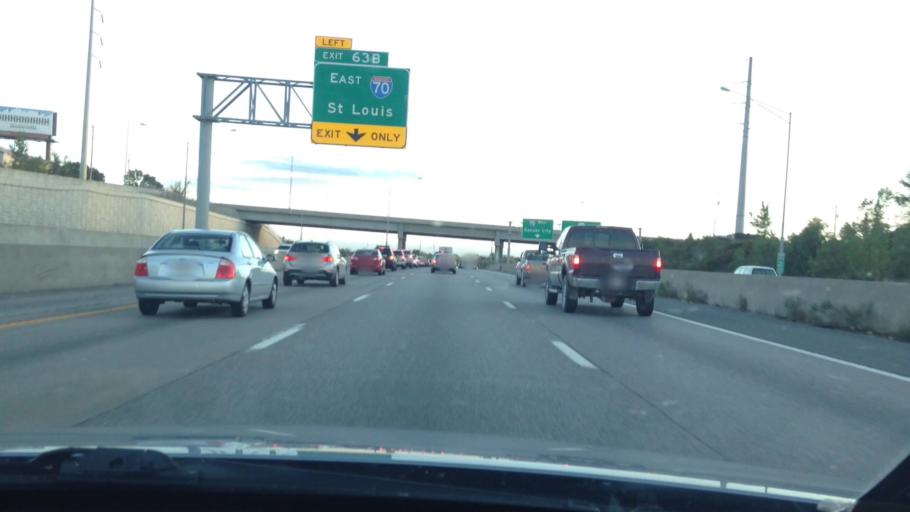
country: US
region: Missouri
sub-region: Jackson County
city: Raytown
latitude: 39.0652
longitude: -94.4882
